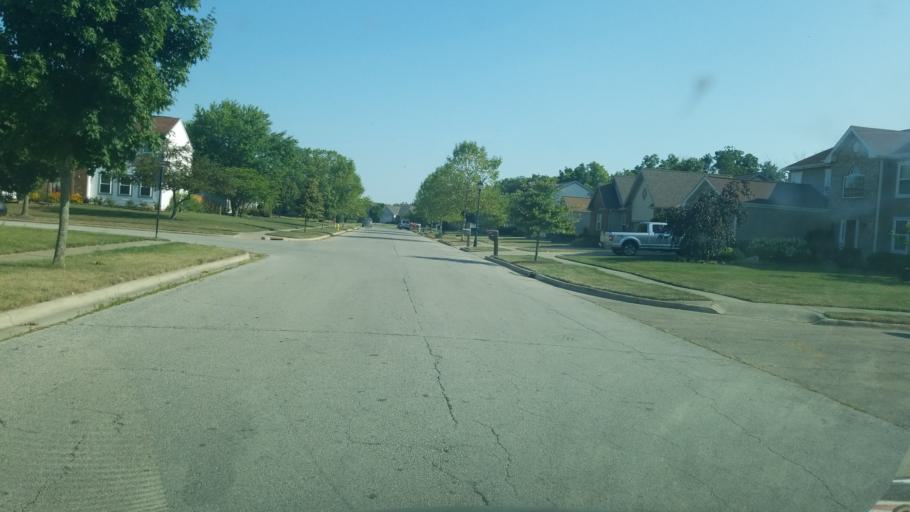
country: US
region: Ohio
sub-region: Franklin County
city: Grove City
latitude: 39.8843
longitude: -83.1144
